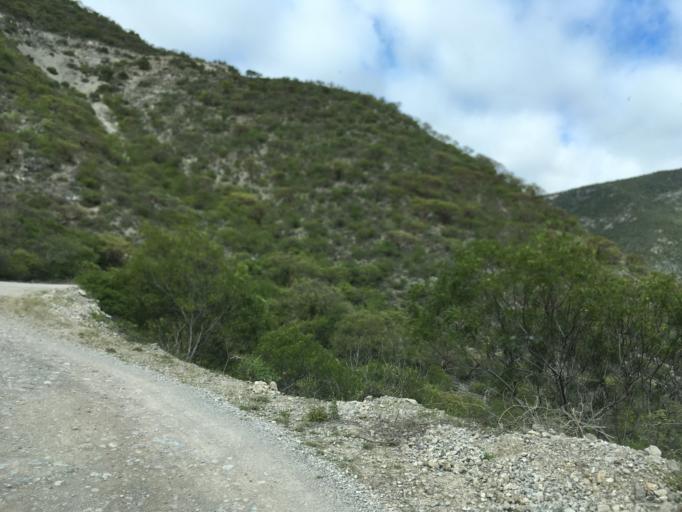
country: MX
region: Hidalgo
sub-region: Metztitlan
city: Fontezuelas
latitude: 20.6389
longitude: -98.9325
